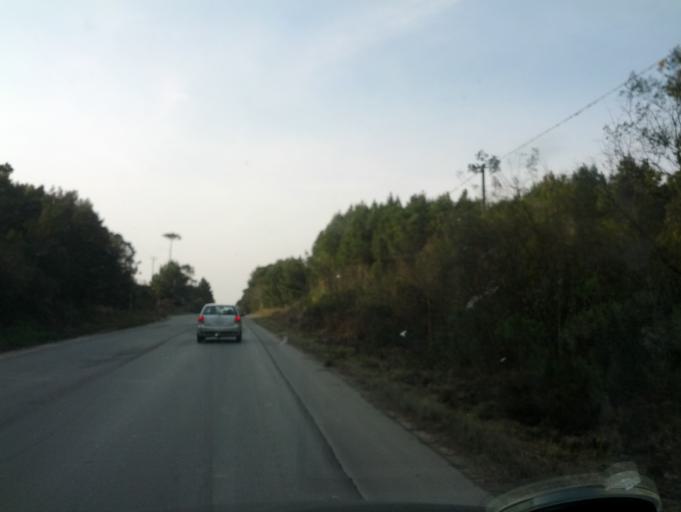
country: BR
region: Santa Catarina
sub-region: Otacilio Costa
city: Otacilio Costa
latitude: -27.5662
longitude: -50.1503
